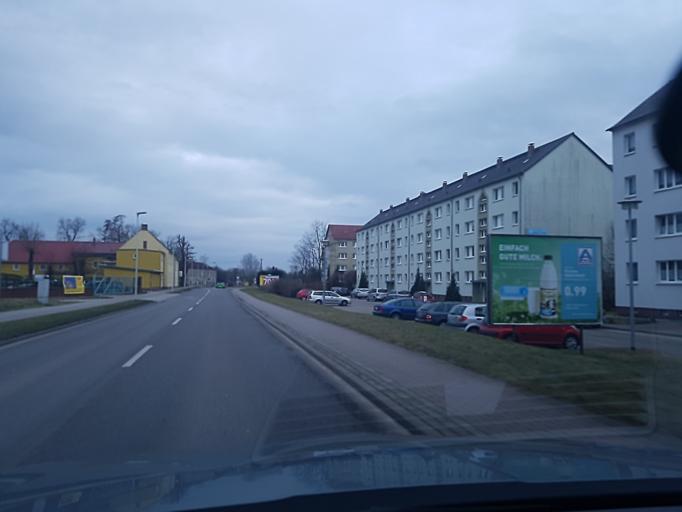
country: DE
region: Brandenburg
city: Doberlug-Kirchhain
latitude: 51.6235
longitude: 13.5625
